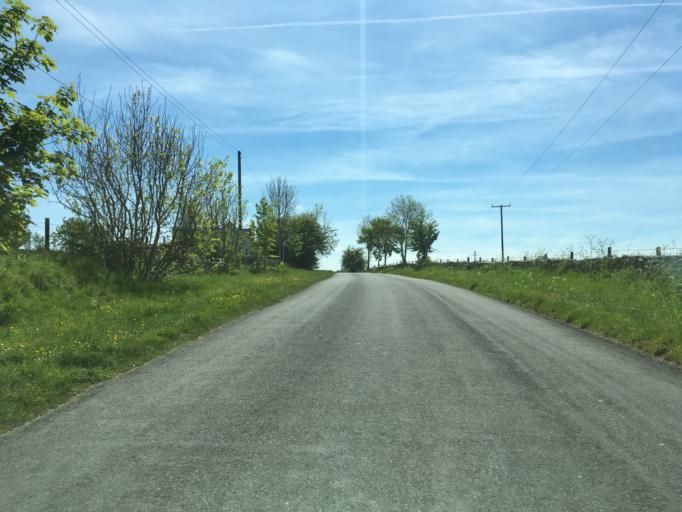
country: GB
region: England
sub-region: Gloucestershire
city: Chalford
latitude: 51.7206
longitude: -2.1169
